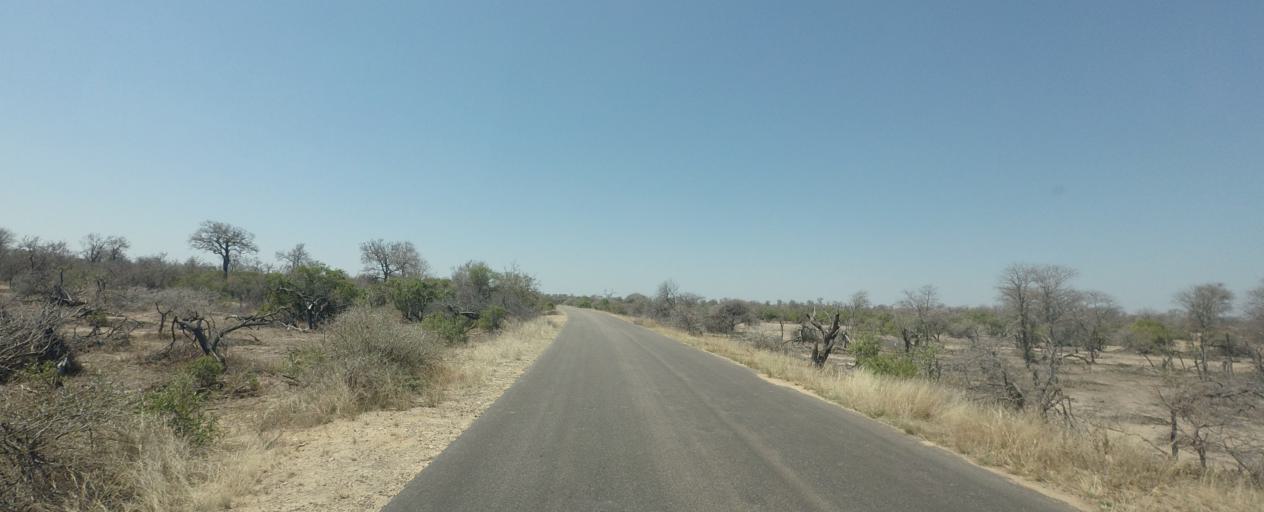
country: ZA
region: Limpopo
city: Thulamahashi
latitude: -24.4354
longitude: 31.4963
